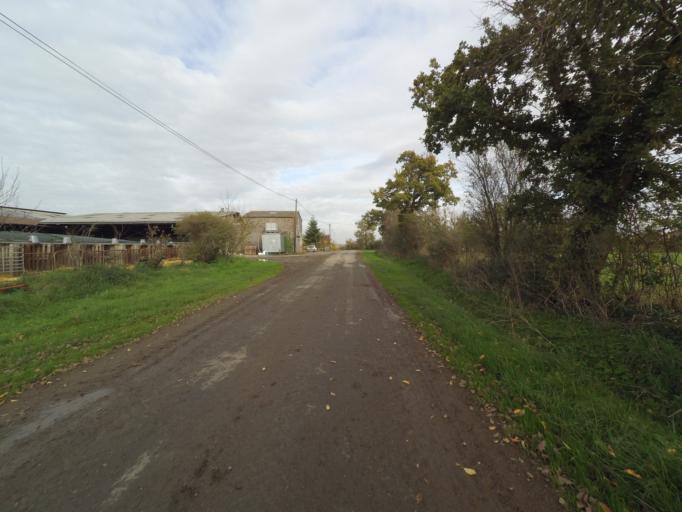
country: FR
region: Pays de la Loire
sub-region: Departement de la Vendee
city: Saint-Hilaire-de-Loulay
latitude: 47.0328
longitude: -1.3414
